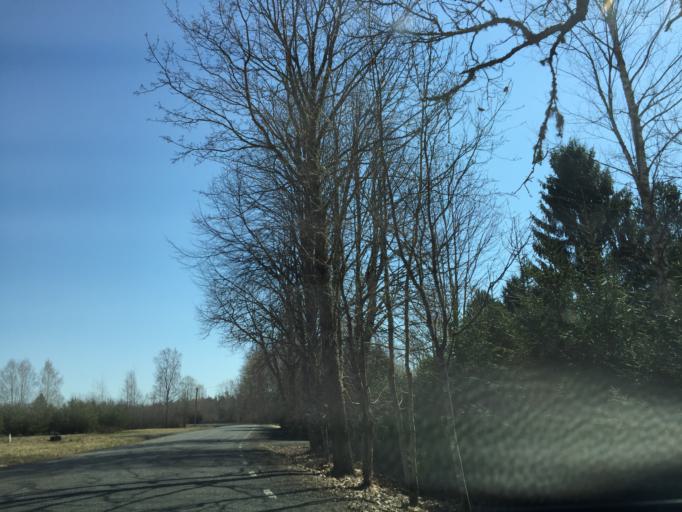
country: EE
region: Tartu
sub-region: Alatskivi vald
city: Kallaste
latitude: 58.5769
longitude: 26.9186
